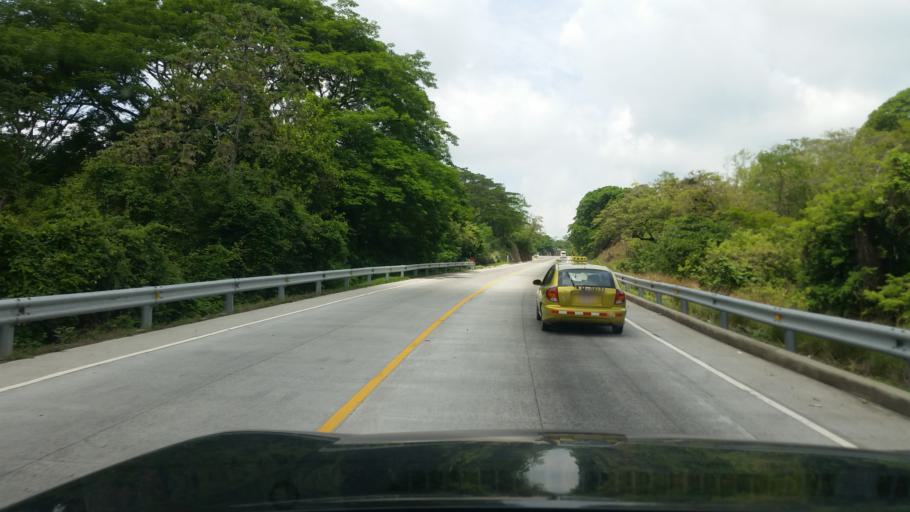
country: NI
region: Managua
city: Ciudad Sandino
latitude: 12.0835
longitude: -86.3876
